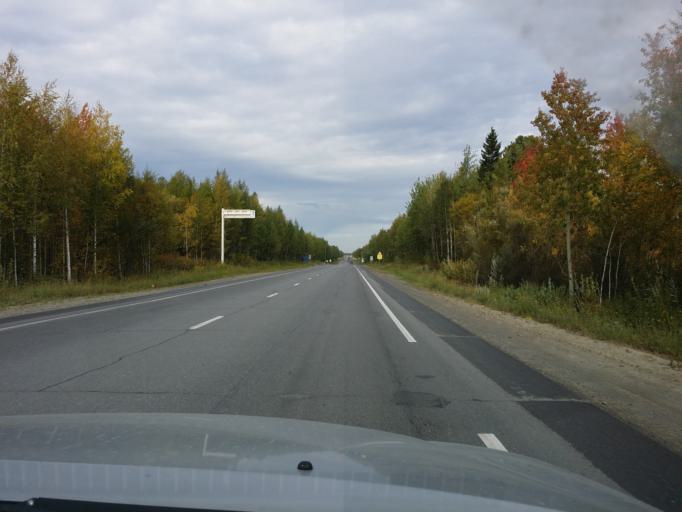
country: RU
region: Khanty-Mansiyskiy Avtonomnyy Okrug
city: Megion
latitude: 61.0583
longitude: 76.2936
